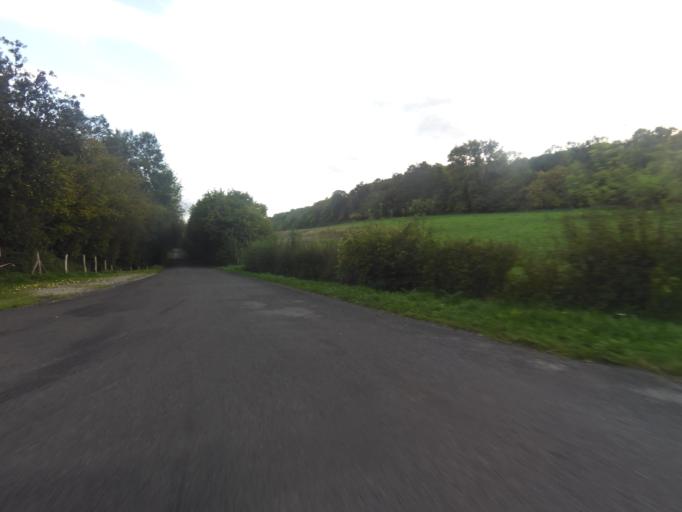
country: FR
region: Lower Normandy
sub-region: Departement de l'Orne
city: Vimoutiers
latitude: 48.9557
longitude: 0.2639
